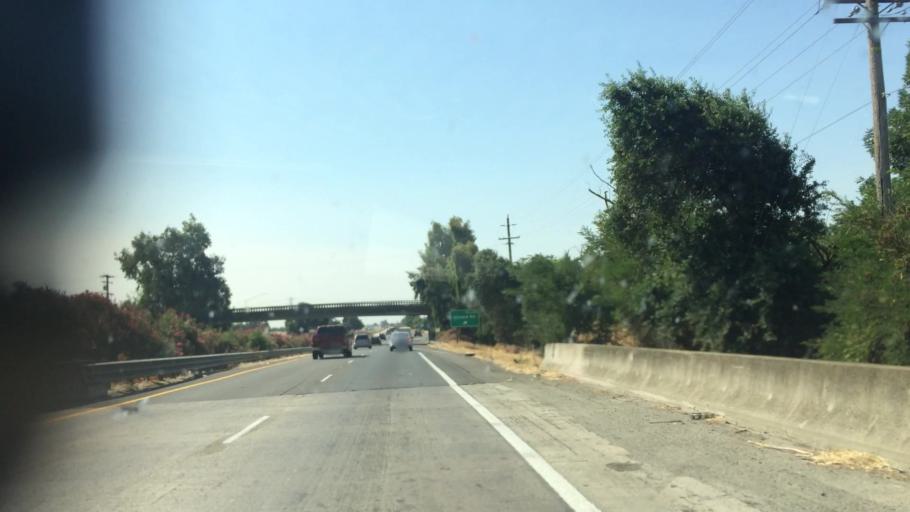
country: US
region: California
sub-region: Sacramento County
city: Elk Grove
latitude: 38.3445
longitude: -121.3363
